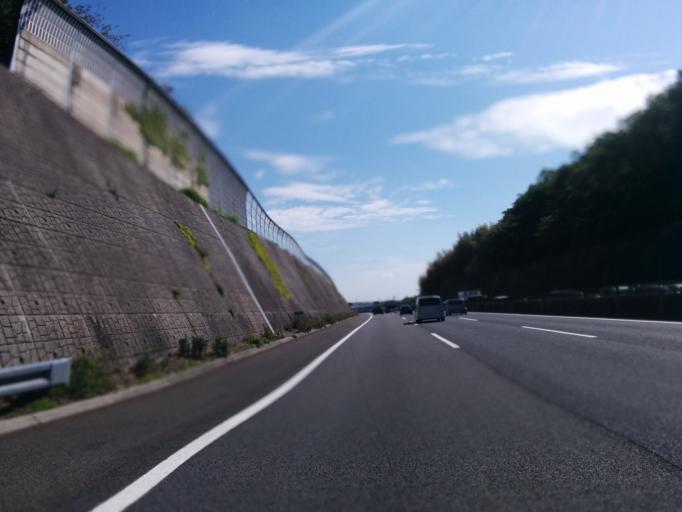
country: JP
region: Mie
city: Yokkaichi
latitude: 35.0214
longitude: 136.5972
